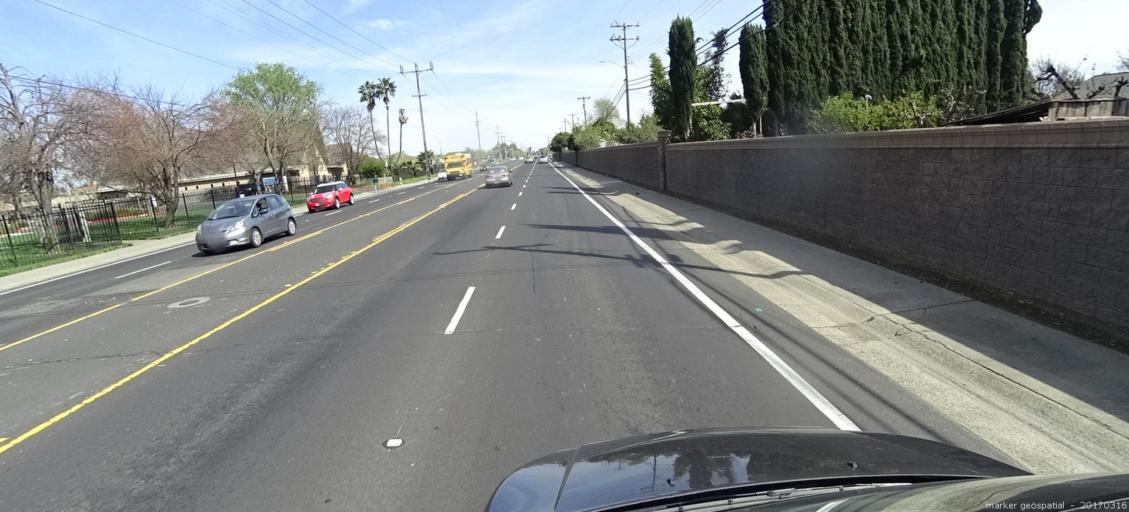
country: US
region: California
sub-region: Sacramento County
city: Parkway
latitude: 38.4814
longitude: -121.4847
